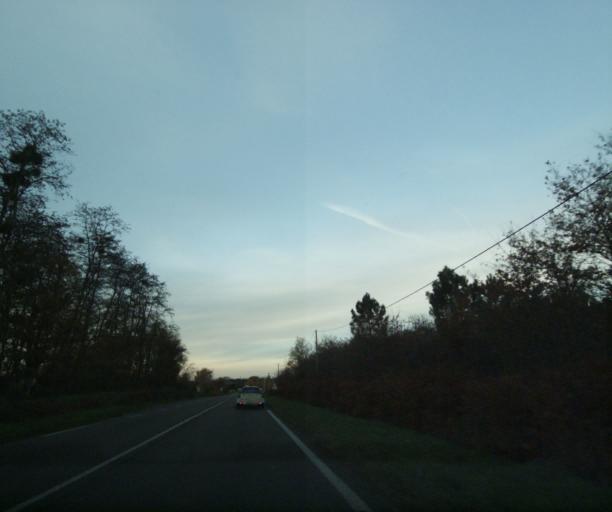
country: FR
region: Aquitaine
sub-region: Departement de la Gironde
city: Langon
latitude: 44.4966
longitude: -0.2367
